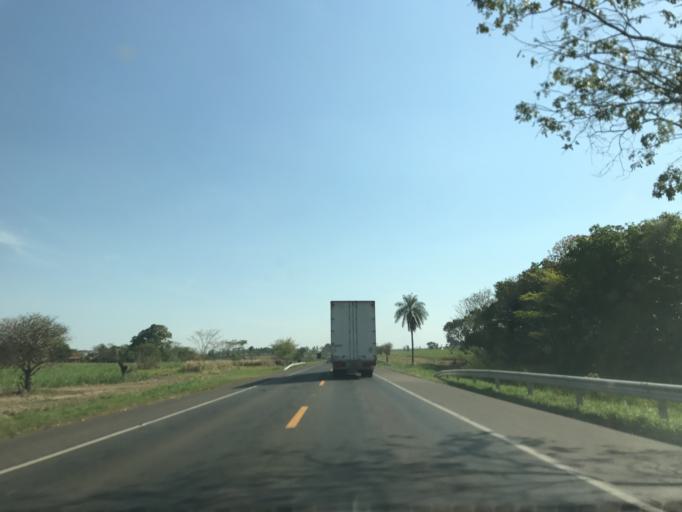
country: BR
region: Sao Paulo
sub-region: Penapolis
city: Penapolis
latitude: -21.4638
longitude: -50.1789
